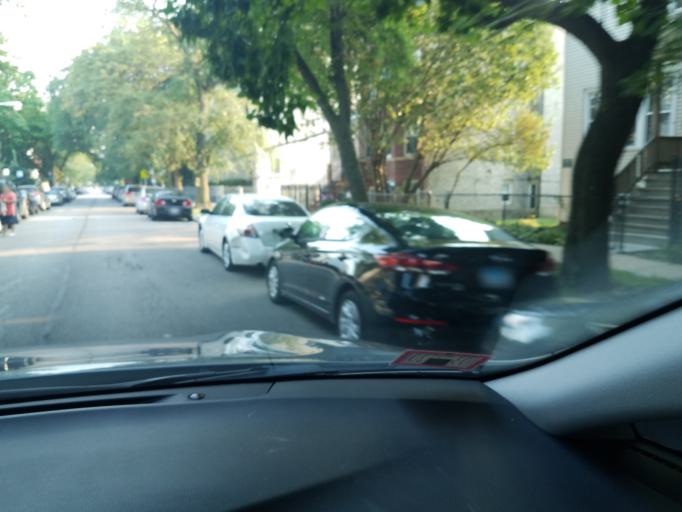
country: US
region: Illinois
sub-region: Cook County
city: Chicago
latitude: 41.9166
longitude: -87.7005
